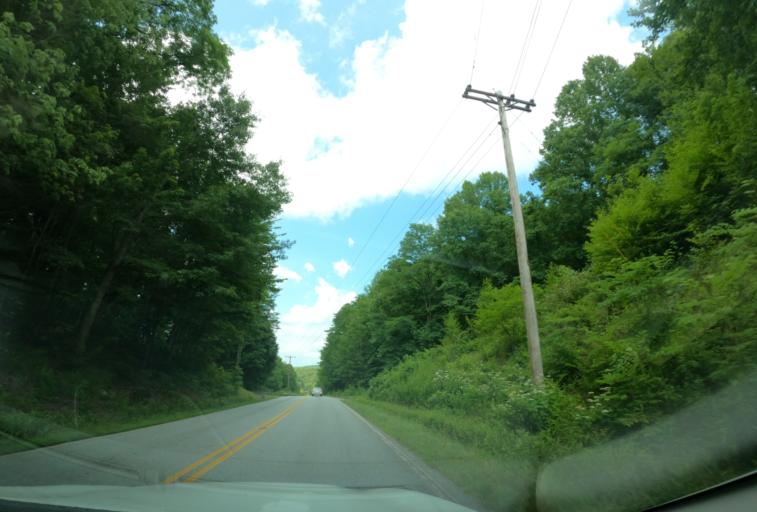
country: US
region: North Carolina
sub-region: Transylvania County
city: Brevard
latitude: 35.0847
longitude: -82.9865
